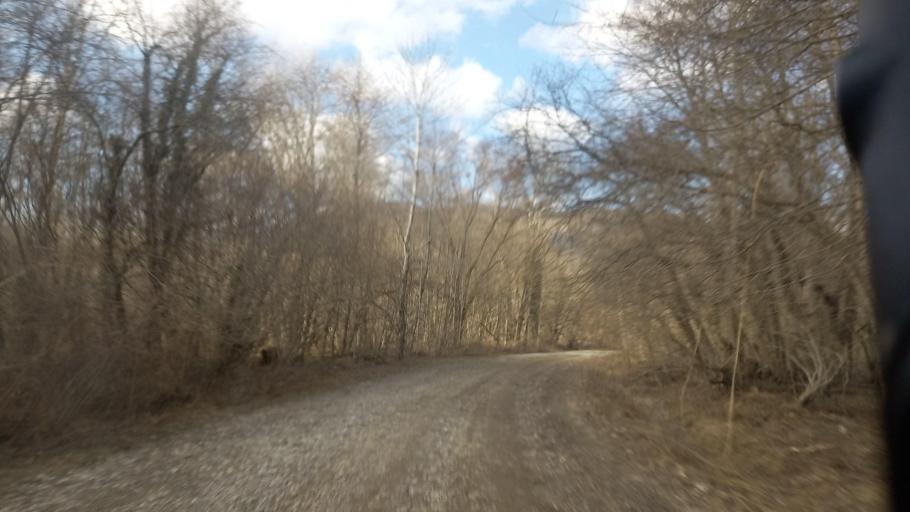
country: RU
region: Krasnodarskiy
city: Smolenskaya
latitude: 44.6207
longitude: 38.8246
